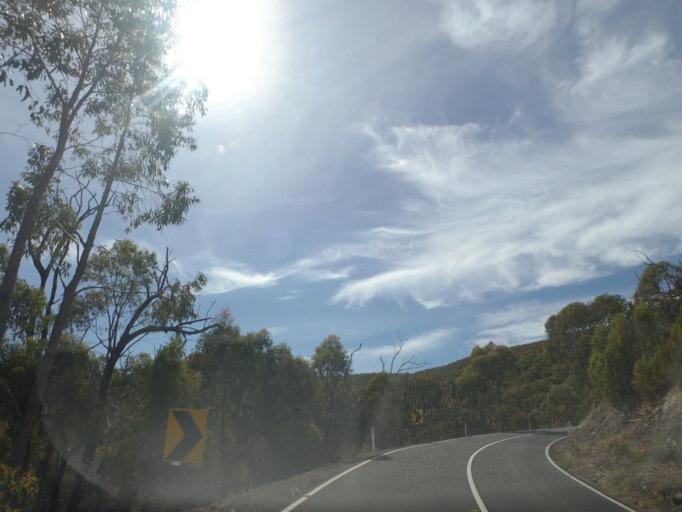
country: AU
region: Victoria
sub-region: Nillumbik
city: Saint Andrews
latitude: -37.5595
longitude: 145.3239
